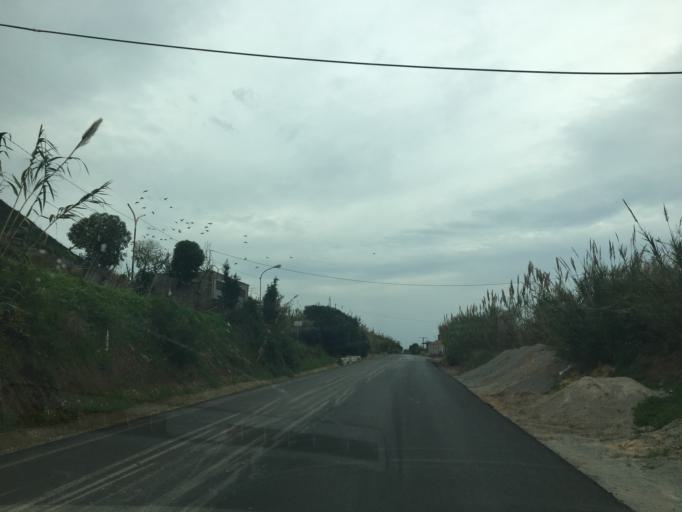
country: DZ
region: Tipaza
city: Tipasa
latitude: 36.6390
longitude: 2.3316
